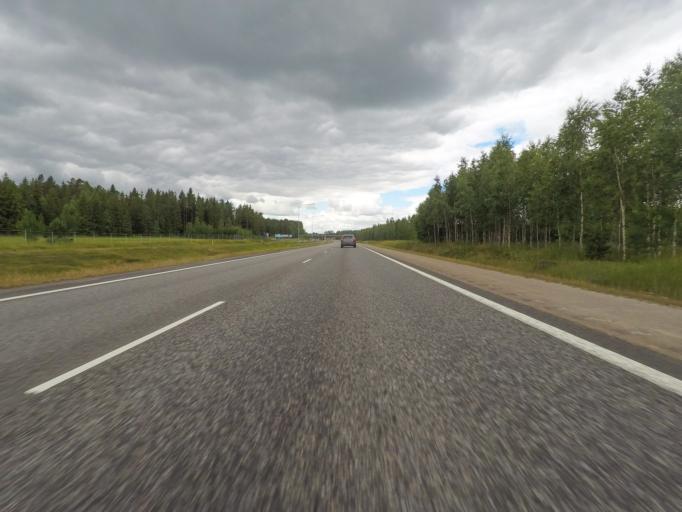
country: FI
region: Varsinais-Suomi
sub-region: Turku
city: Piikkioe
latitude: 60.4467
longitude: 22.5133
